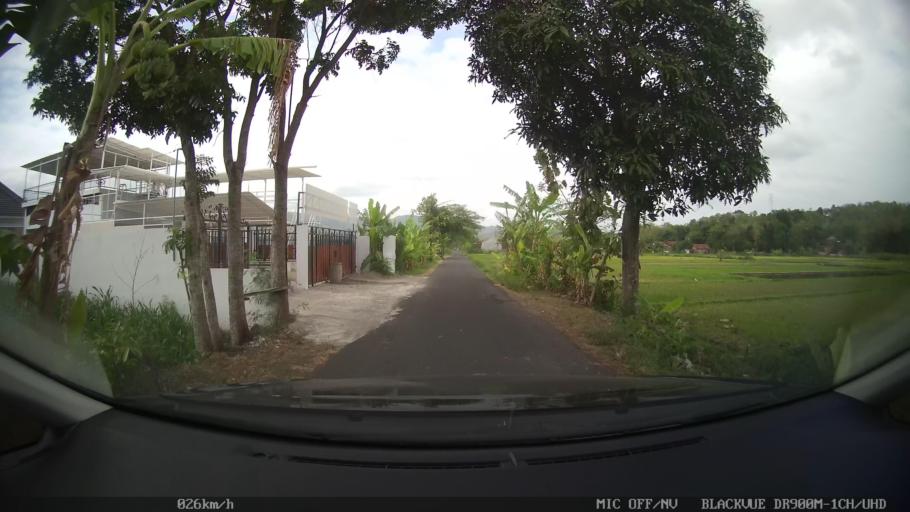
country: ID
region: Daerah Istimewa Yogyakarta
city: Depok
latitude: -7.8227
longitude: 110.4641
